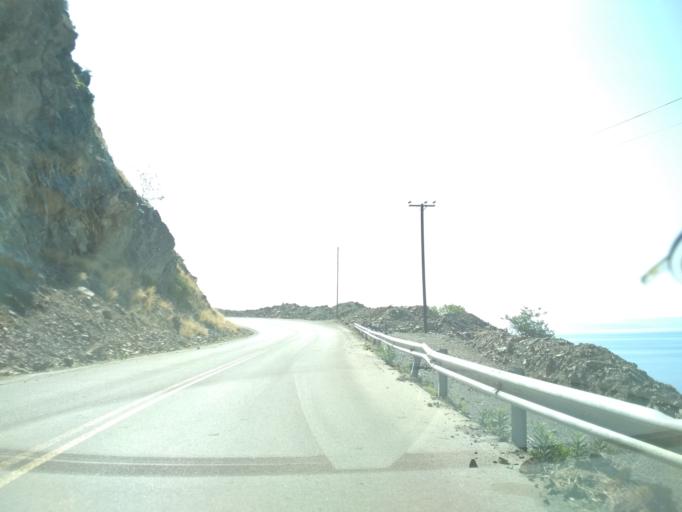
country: GR
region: Central Greece
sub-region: Nomos Evvoias
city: Roviai
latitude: 38.8477
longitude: 23.1571
